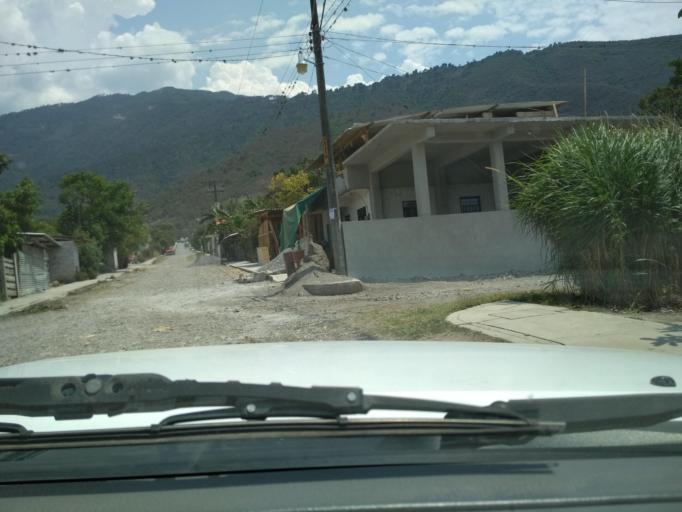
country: MX
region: Veracruz
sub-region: Acultzingo
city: Acatla
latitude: 18.7506
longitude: -97.2202
